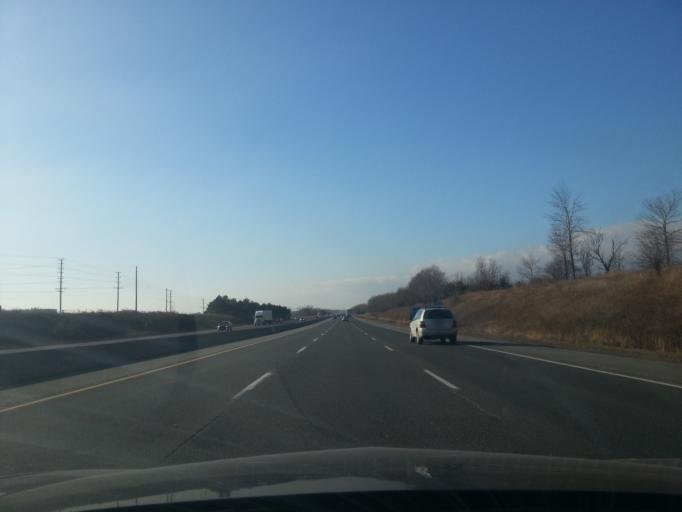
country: CA
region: Ontario
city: Oshawa
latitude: 43.8818
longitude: -78.7408
